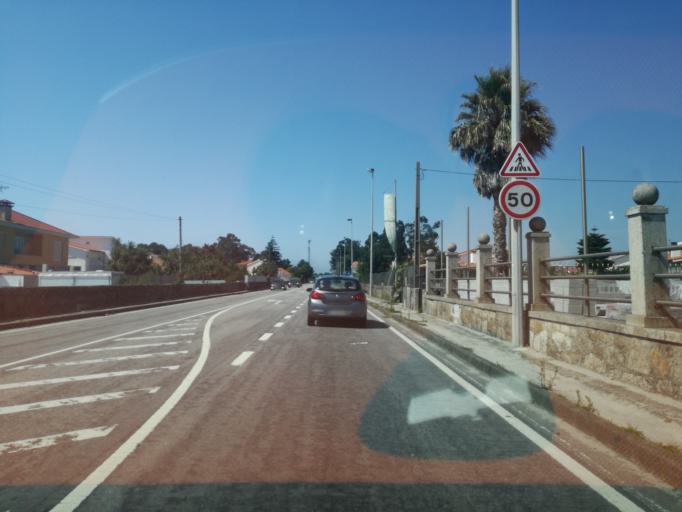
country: PT
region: Braga
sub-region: Esposende
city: Esposende
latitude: 41.5342
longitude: -8.7777
